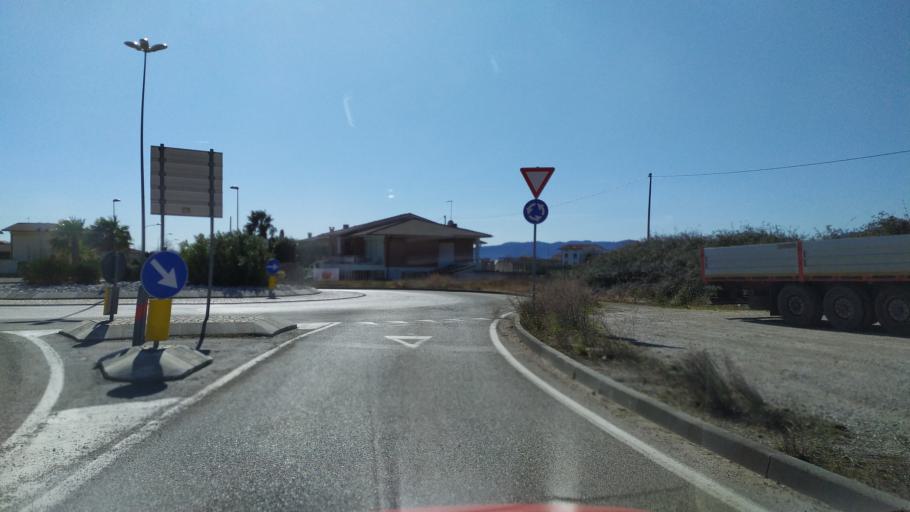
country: IT
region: Veneto
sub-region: Provincia di Vicenza
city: Carre
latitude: 45.7556
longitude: 11.4580
